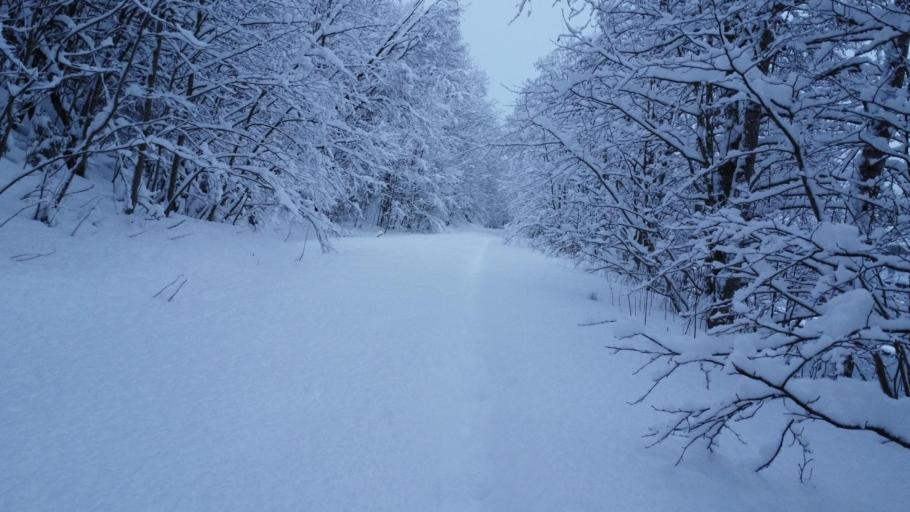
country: NO
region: Nordland
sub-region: Rana
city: Mo i Rana
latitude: 66.3350
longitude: 14.1574
